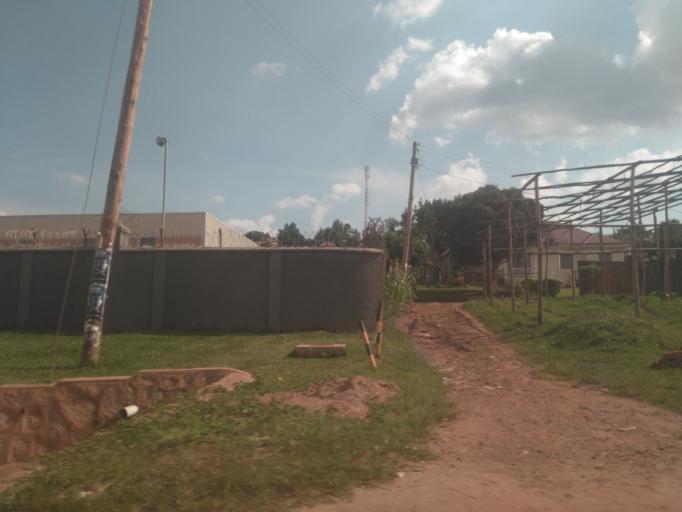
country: UG
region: Central Region
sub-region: Wakiso District
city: Kajansi
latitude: 0.2793
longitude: 32.4710
